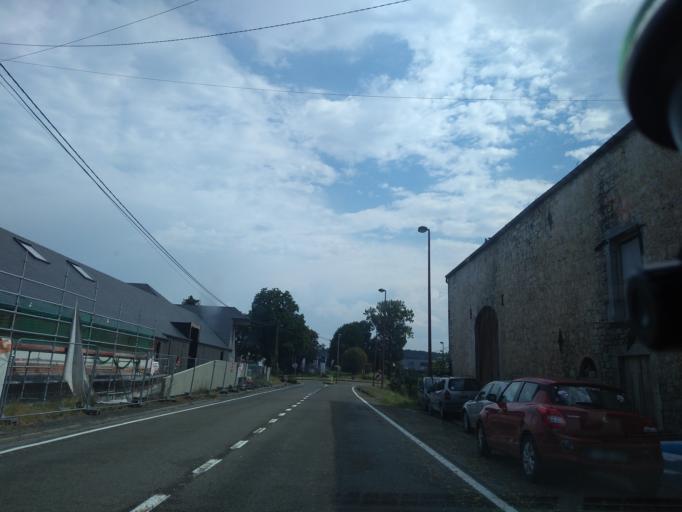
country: BE
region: Wallonia
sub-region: Province de Namur
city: Beauraing
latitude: 50.1212
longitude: 4.9542
